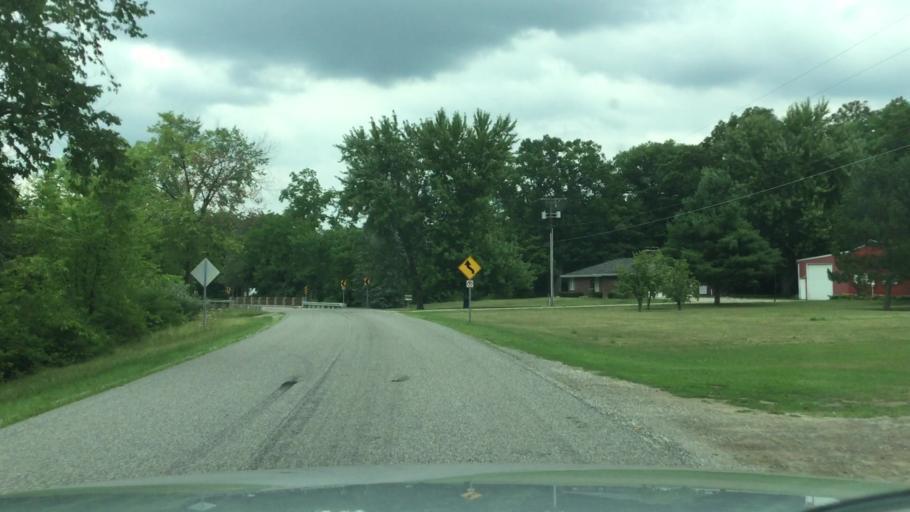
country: US
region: Michigan
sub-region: Saginaw County
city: Burt
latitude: 43.2521
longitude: -83.8672
